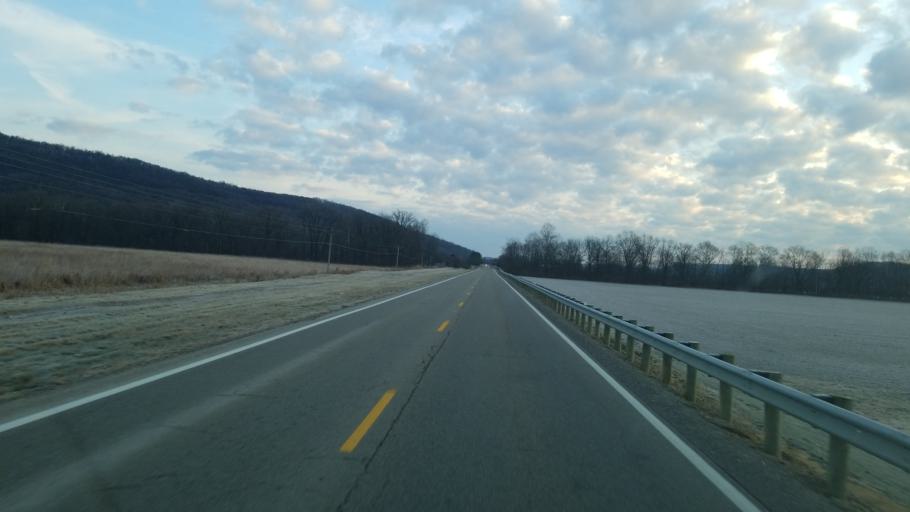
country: US
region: Ohio
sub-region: Ross County
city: Frankfort
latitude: 39.2380
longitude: -83.2346
